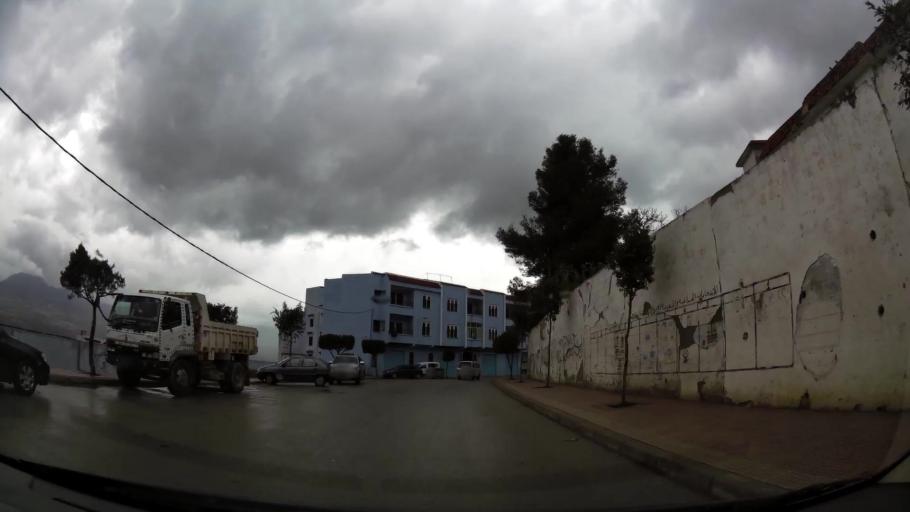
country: MA
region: Tanger-Tetouan
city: Chefchaouene
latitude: 35.1678
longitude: -5.2713
